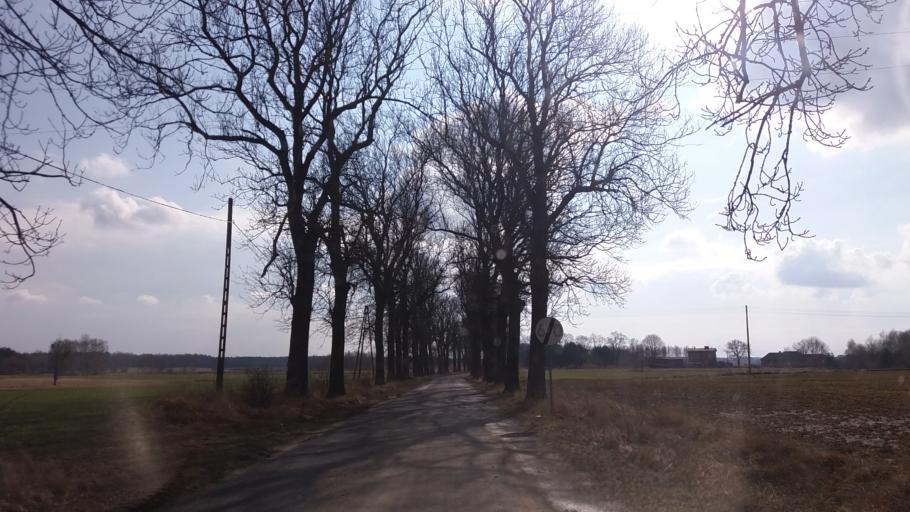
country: PL
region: West Pomeranian Voivodeship
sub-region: Powiat choszczenski
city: Recz
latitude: 53.1768
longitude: 15.6053
